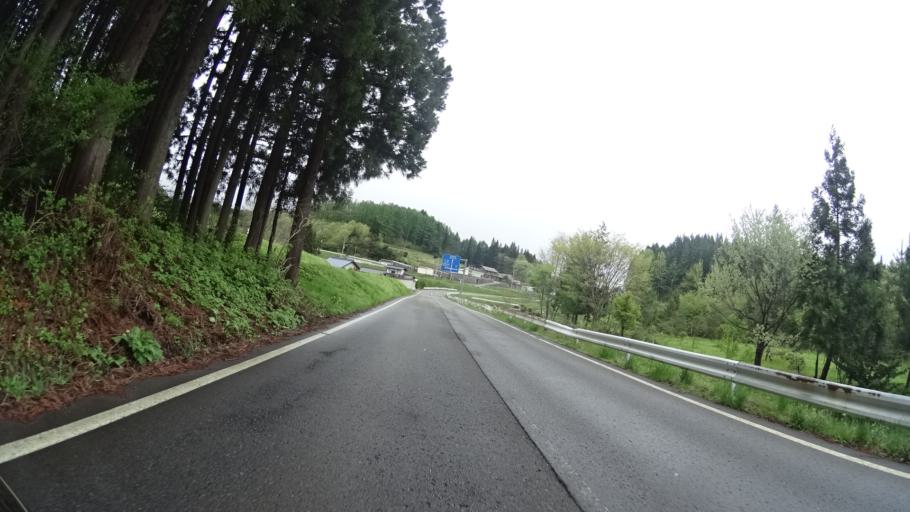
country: JP
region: Nagano
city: Nagano-shi
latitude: 36.7558
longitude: 138.1983
